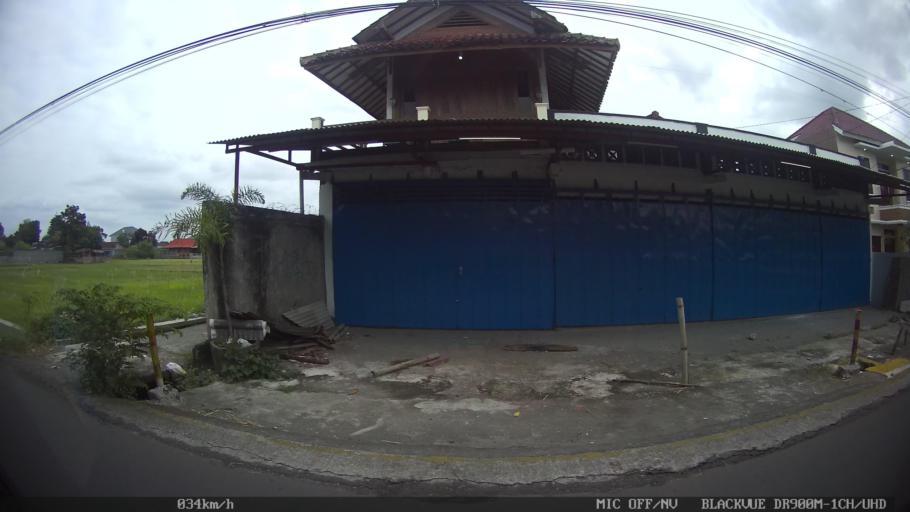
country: ID
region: Daerah Istimewa Yogyakarta
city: Depok
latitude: -7.8295
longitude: 110.4156
